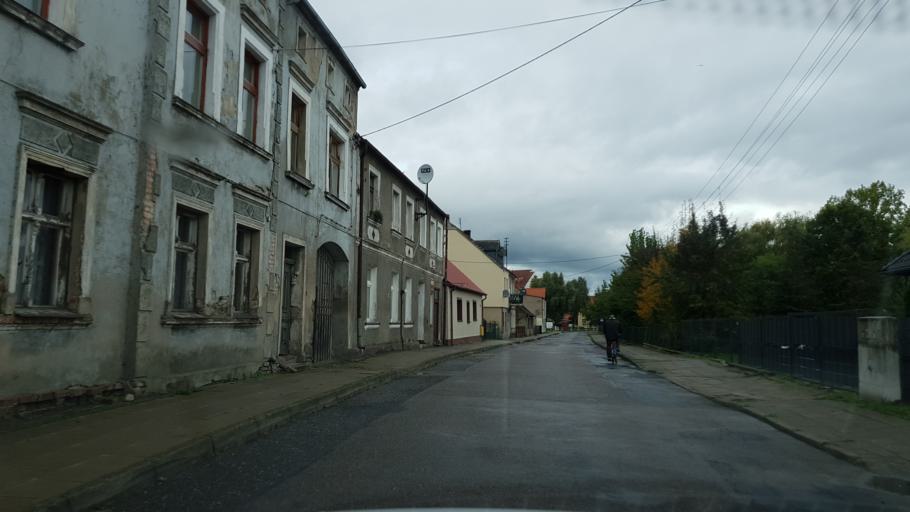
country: PL
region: West Pomeranian Voivodeship
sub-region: Powiat kamienski
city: Wolin
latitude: 53.8397
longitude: 14.6146
